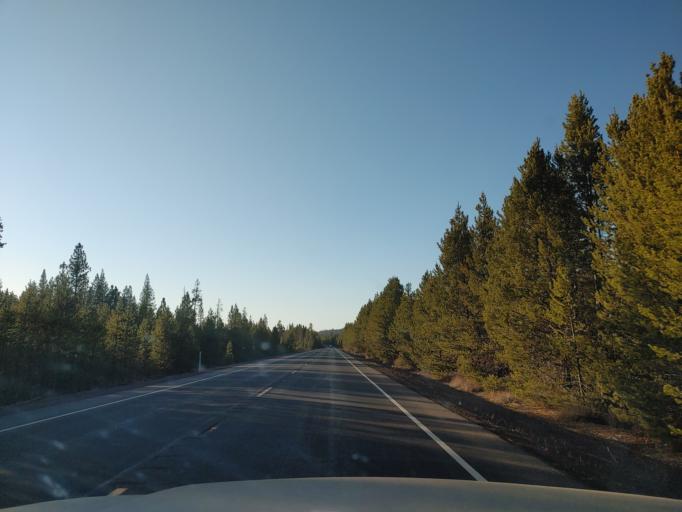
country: US
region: Oregon
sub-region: Deschutes County
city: La Pine
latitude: 43.4156
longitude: -121.8361
